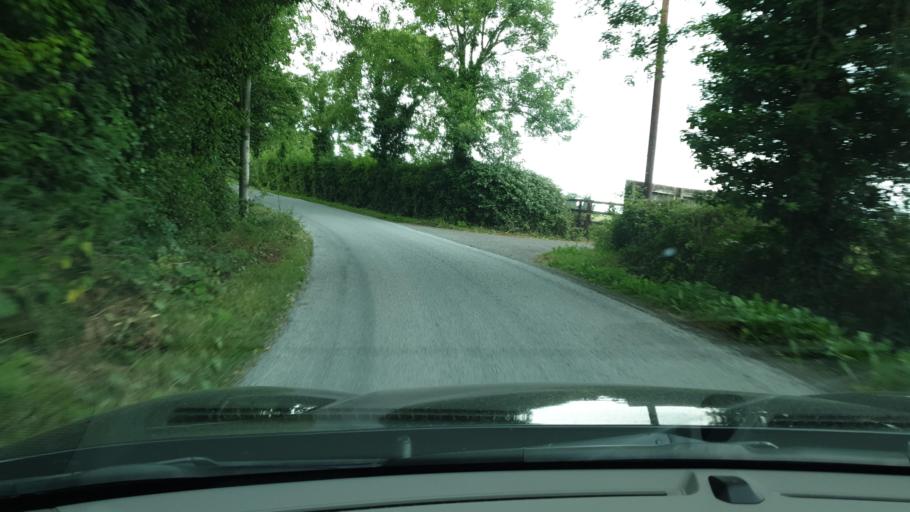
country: IE
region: Leinster
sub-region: An Mhi
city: Ratoath
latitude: 53.4923
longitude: -6.4992
